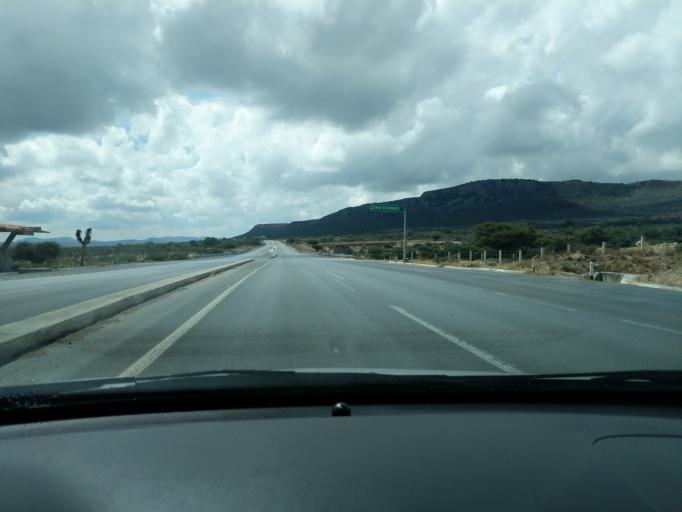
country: MX
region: Zacatecas
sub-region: Pinos
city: Santiago
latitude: 22.4054
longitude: -101.3888
